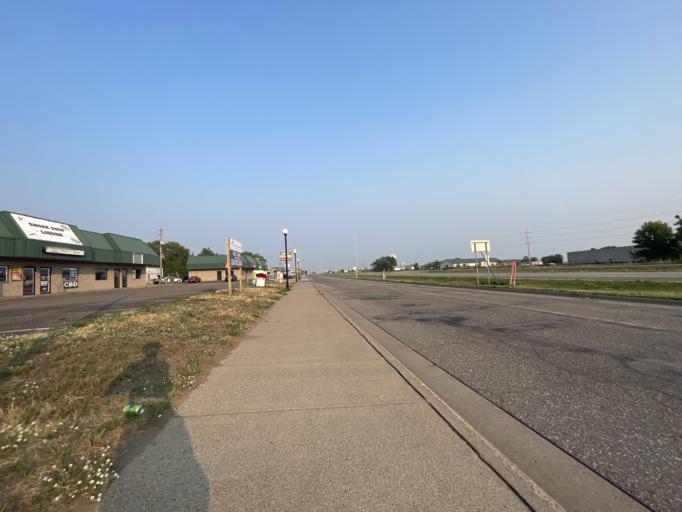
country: US
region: Minnesota
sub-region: Sherburne County
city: Becker
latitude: 45.3916
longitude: -93.8744
